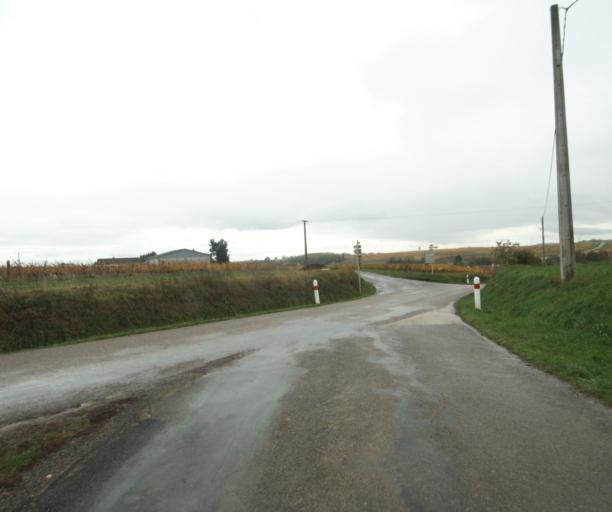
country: FR
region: Rhone-Alpes
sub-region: Departement de l'Ain
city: Pont-de-Vaux
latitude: 46.4788
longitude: 4.8598
